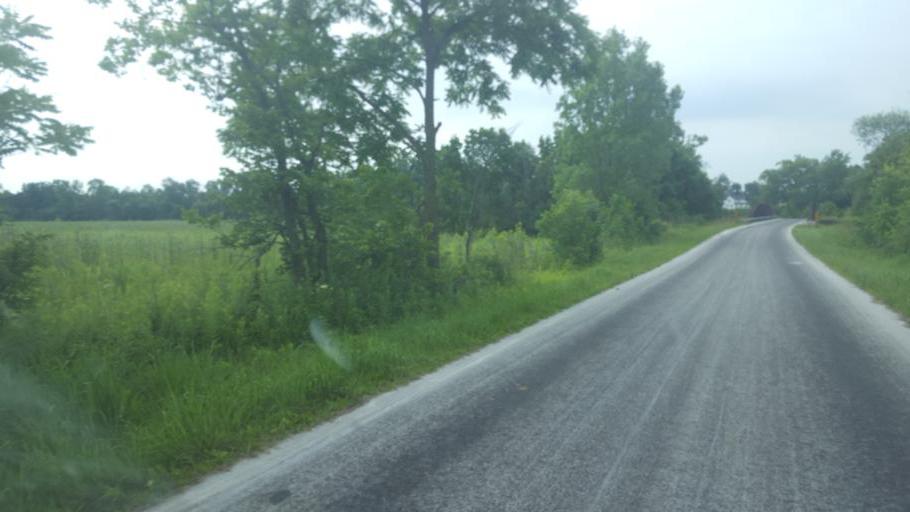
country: US
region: Ohio
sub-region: Hardin County
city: Kenton
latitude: 40.6229
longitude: -83.5302
